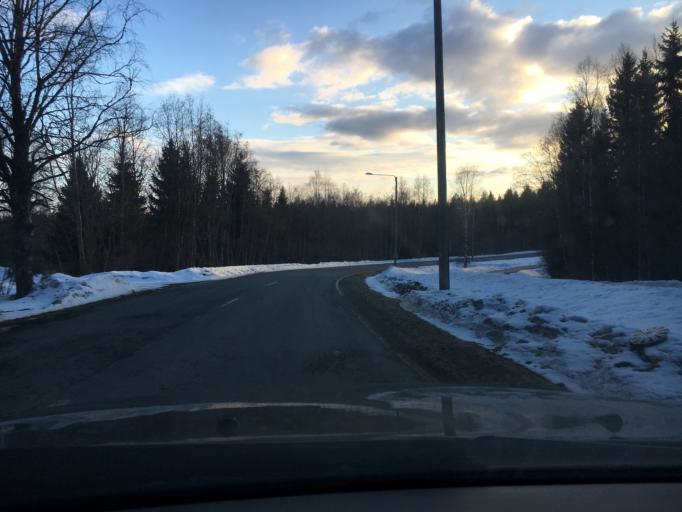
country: FI
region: Kainuu
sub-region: Kajaani
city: Kajaani
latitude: 64.2650
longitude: 27.7630
